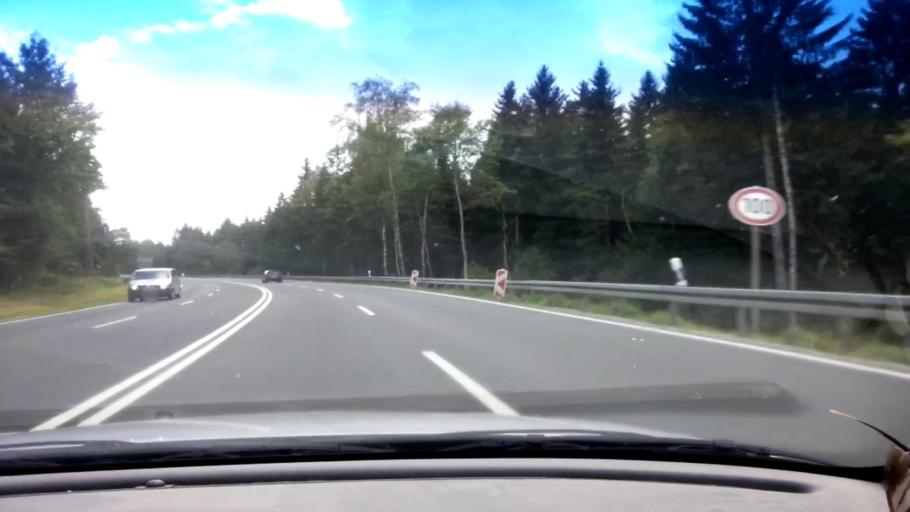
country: DE
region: Bavaria
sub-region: Upper Franconia
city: Trostau
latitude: 50.0138
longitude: 11.9273
